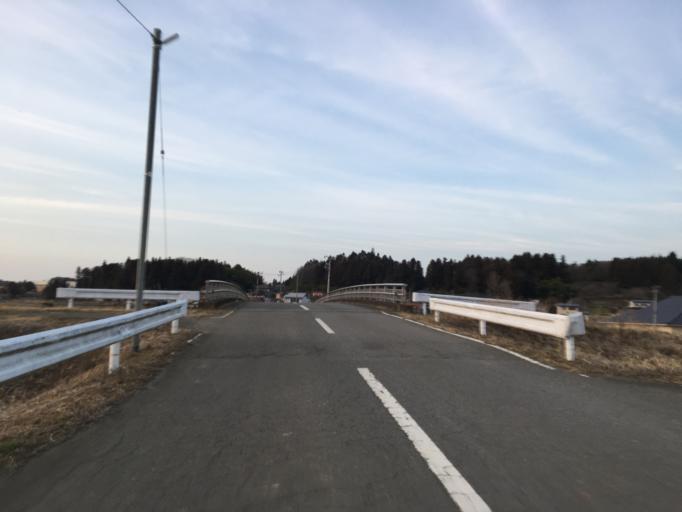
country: JP
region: Fukushima
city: Ishikawa
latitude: 37.0626
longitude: 140.3486
